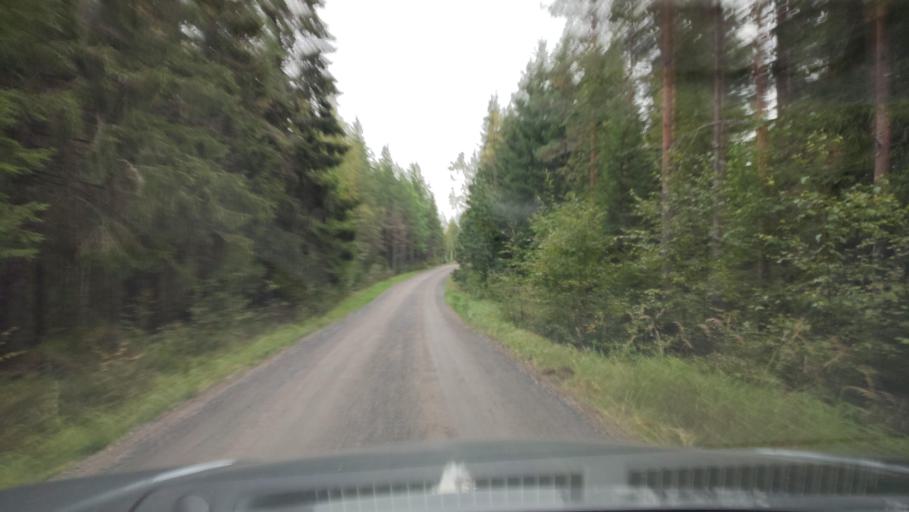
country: FI
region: Southern Ostrobothnia
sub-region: Suupohja
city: Karijoki
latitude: 62.2071
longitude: 21.5779
